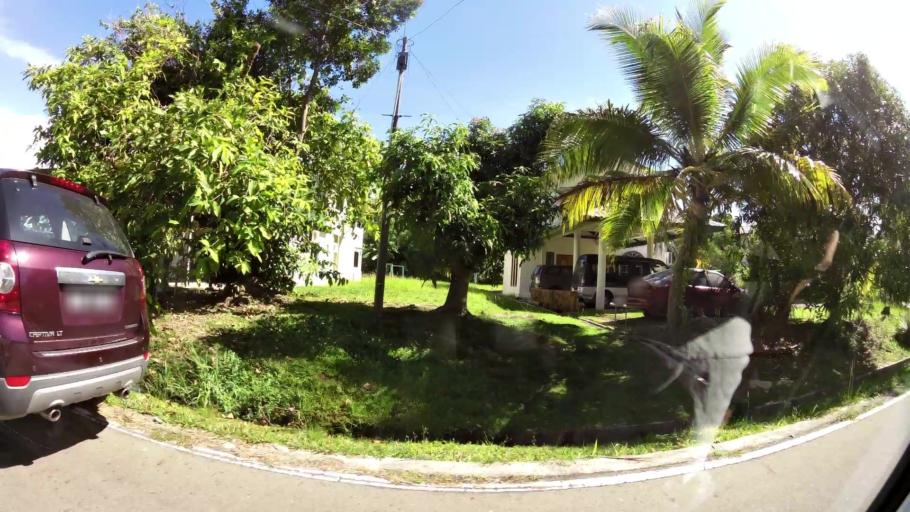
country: BN
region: Brunei and Muara
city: Bandar Seri Begawan
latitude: 5.0038
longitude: 115.0472
